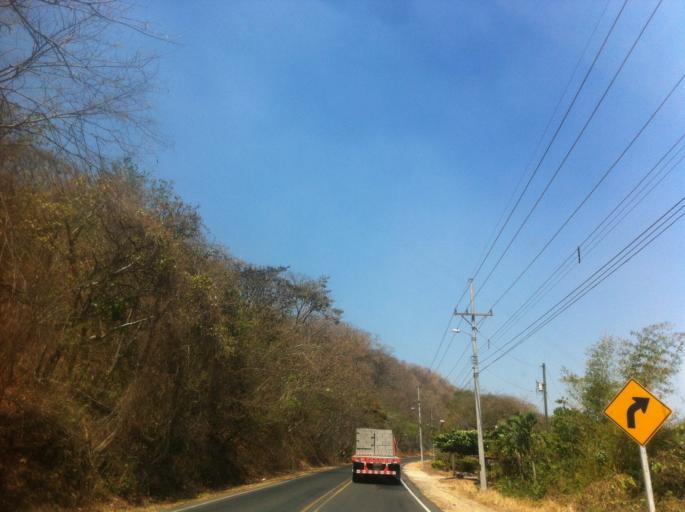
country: CR
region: Guanacaste
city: Santa Cruz
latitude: 10.2215
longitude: -85.5244
